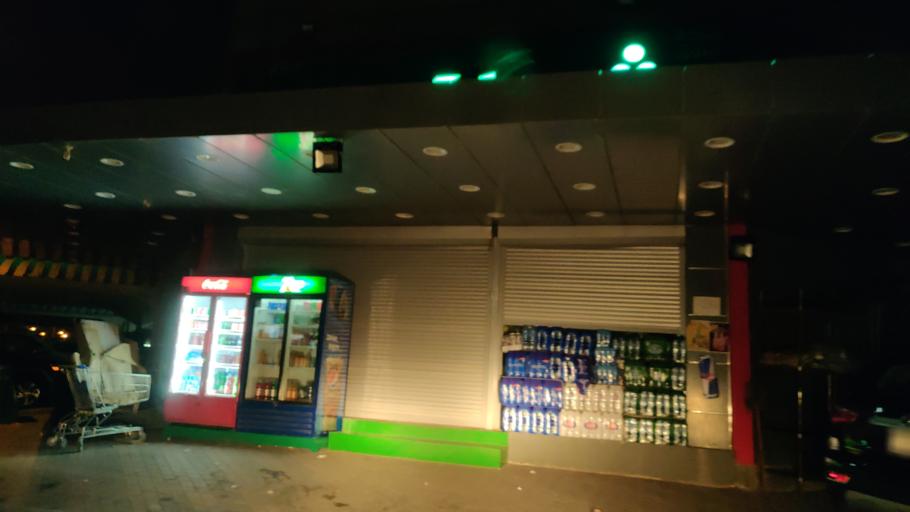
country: KW
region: Muhafazat Hawalli
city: Hawalli
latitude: 29.3264
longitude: 48.0489
